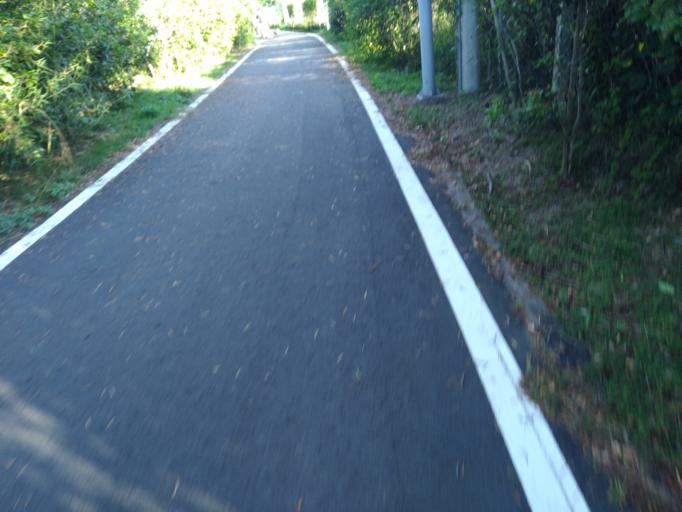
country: TW
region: Taiwan
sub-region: Hsinchu
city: Hsinchu
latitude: 24.7669
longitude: 120.9300
